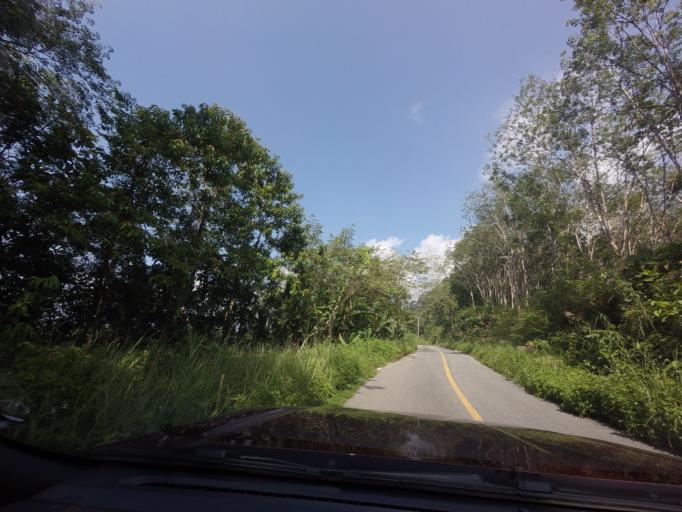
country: TH
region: Yala
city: Than To
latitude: 5.9941
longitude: 101.2092
